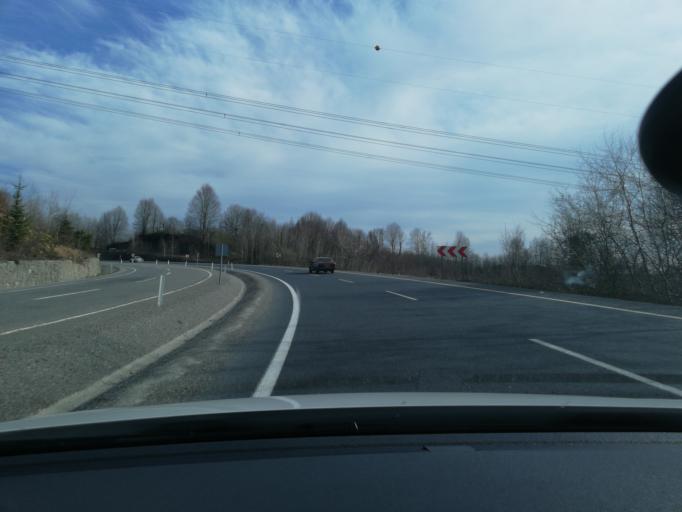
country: TR
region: Zonguldak
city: Ormanli
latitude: 41.3311
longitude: 31.5985
